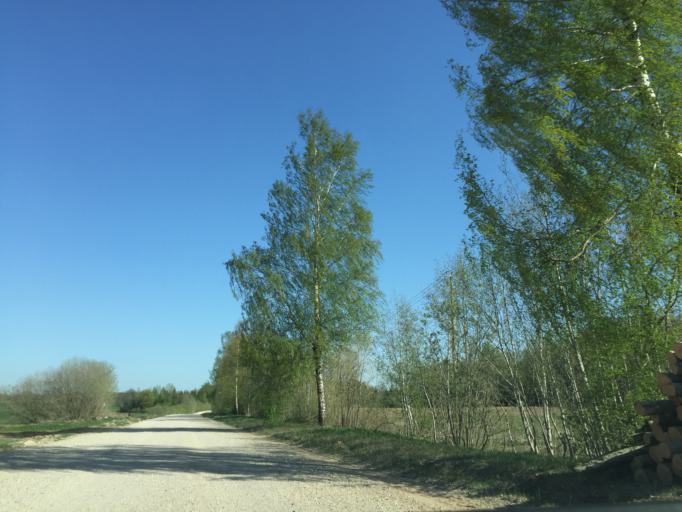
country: LV
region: Malpils
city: Malpils
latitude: 56.8500
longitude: 25.0683
